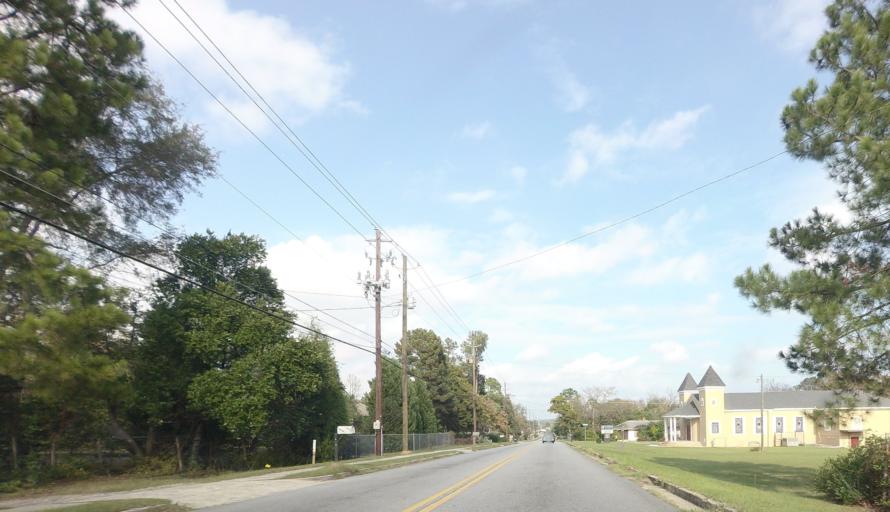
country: US
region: Georgia
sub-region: Bibb County
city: Macon
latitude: 32.8112
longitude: -83.7028
